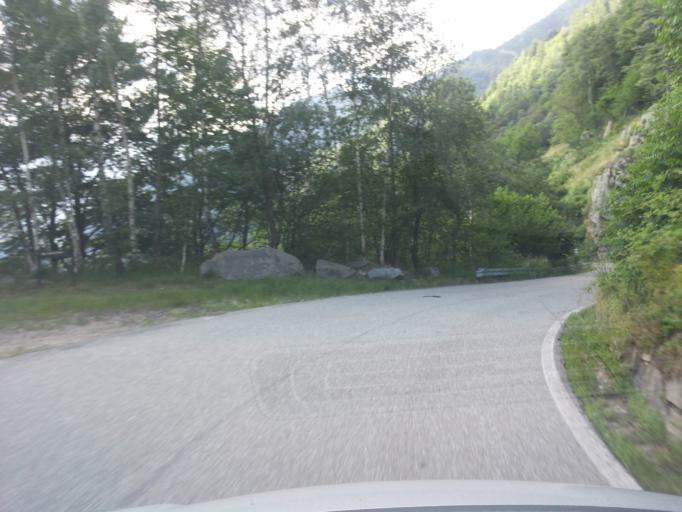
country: IT
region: Piedmont
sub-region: Provincia di Biella
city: Quittengo
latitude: 45.6595
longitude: 8.0167
